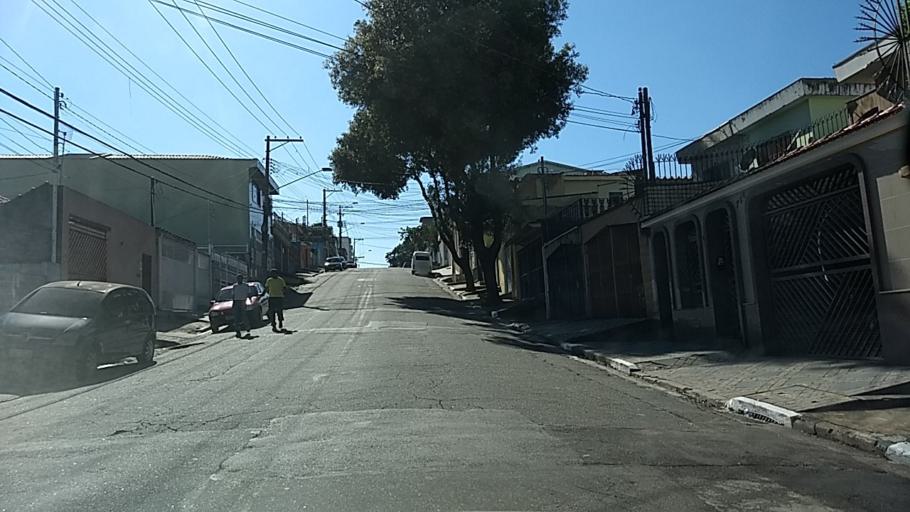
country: BR
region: Sao Paulo
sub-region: Guarulhos
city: Guarulhos
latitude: -23.4901
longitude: -46.5824
